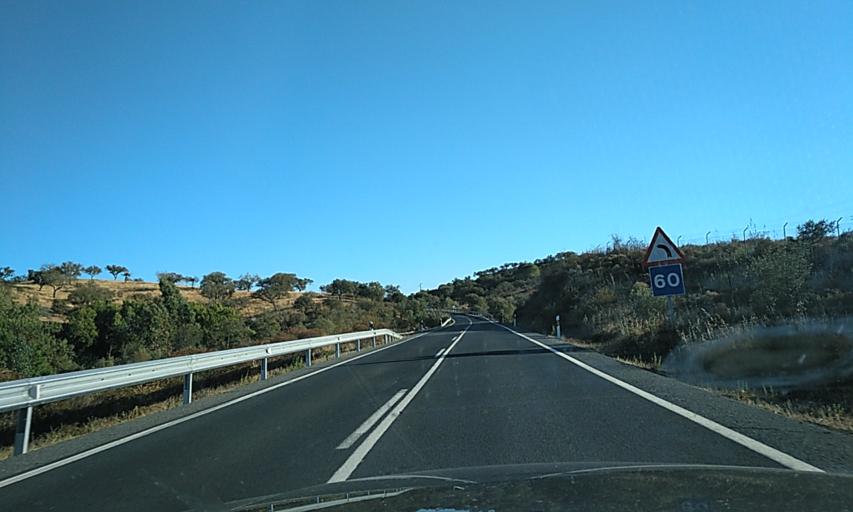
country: ES
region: Andalusia
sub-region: Provincia de Huelva
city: Alosno
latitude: 37.5247
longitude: -7.1350
